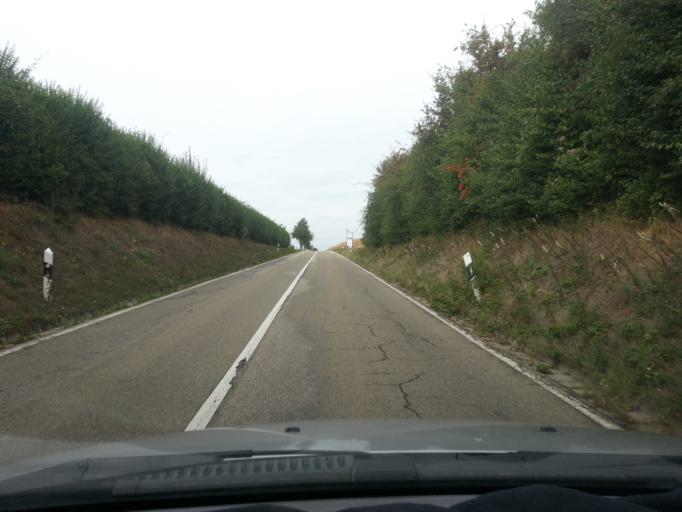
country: DE
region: Rheinland-Pfalz
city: Essingen
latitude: 49.2386
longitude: 8.1741
